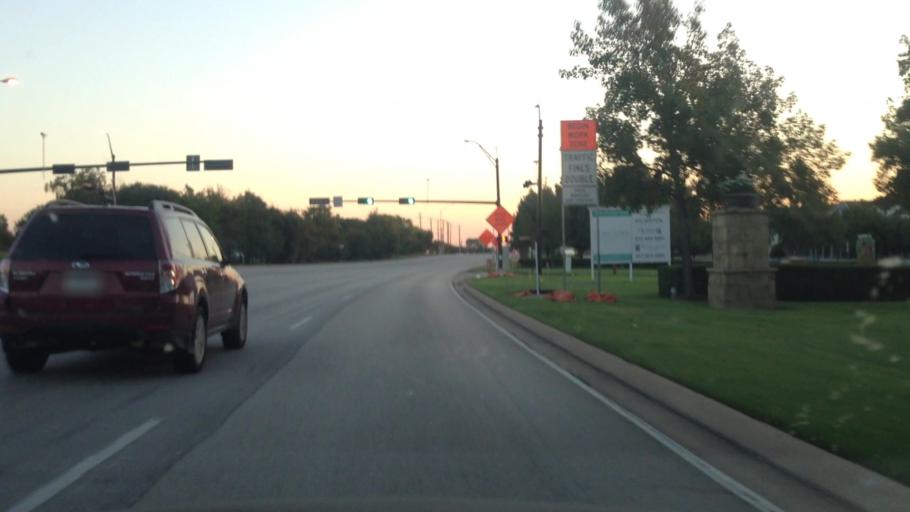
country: US
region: Texas
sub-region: Tarrant County
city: North Richland Hills
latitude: 32.8579
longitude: -97.2117
